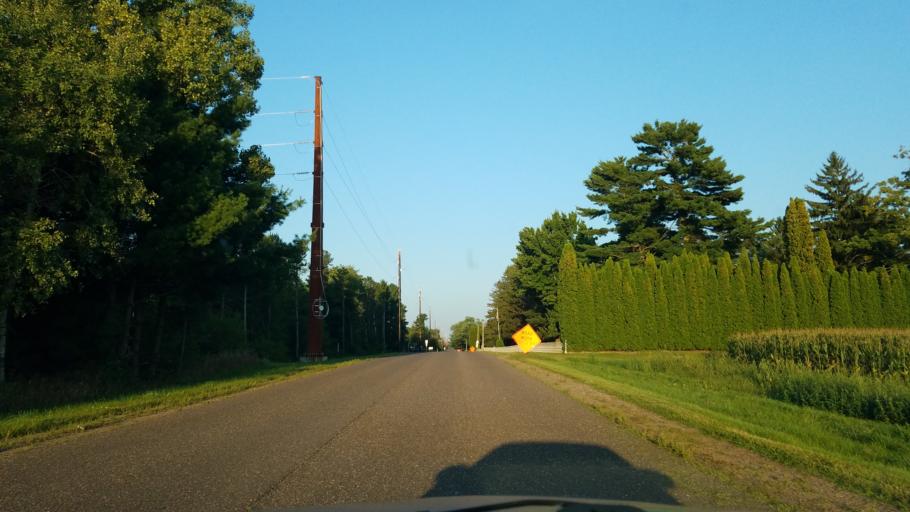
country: US
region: Wisconsin
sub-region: Polk County
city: Clear Lake
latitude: 45.2452
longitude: -92.2771
